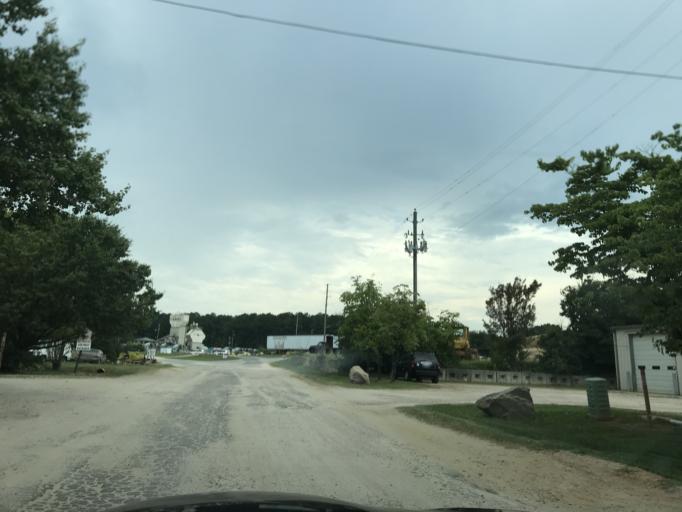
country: US
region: North Carolina
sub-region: Wake County
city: Wake Forest
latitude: 35.8807
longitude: -78.5769
